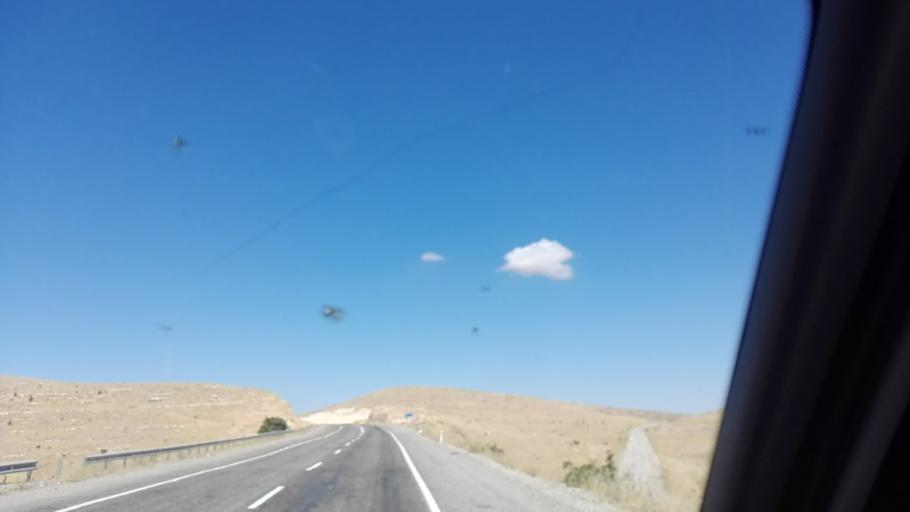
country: TR
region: Batman
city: Gerdzhyush
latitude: 37.5545
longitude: 41.3632
